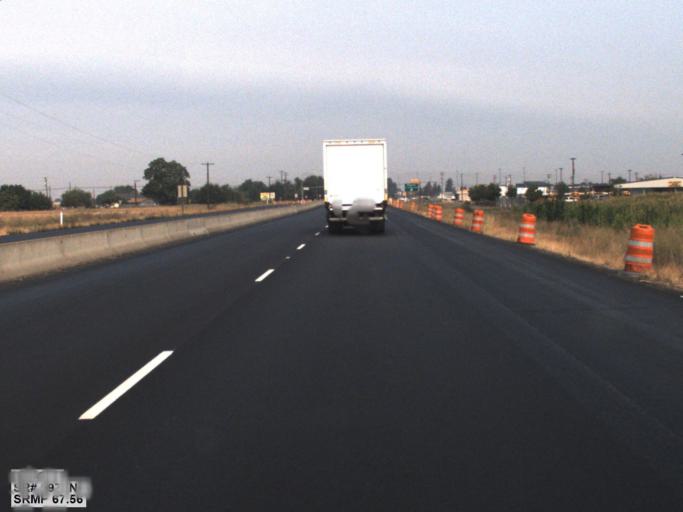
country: US
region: Washington
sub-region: Yakima County
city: Wapato
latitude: 46.4300
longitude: -120.4138
